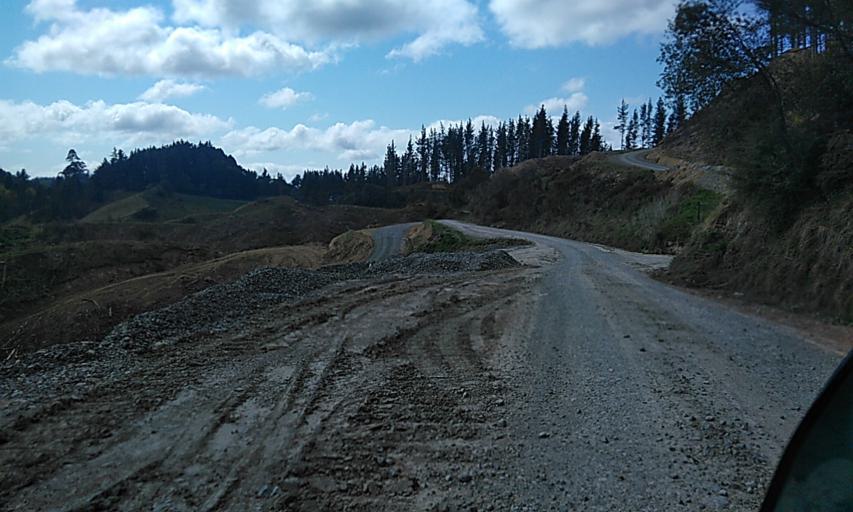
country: NZ
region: Gisborne
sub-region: Gisborne District
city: Gisborne
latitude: -38.3219
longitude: 178.0809
